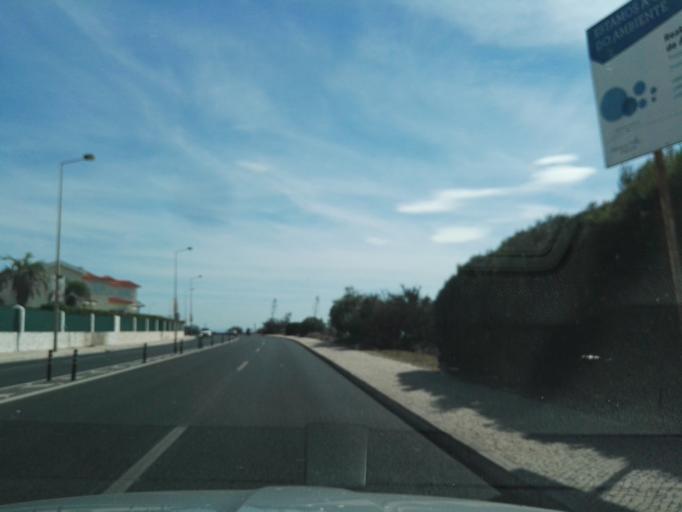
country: PT
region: Lisbon
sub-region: Cascais
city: Parede
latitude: 38.6908
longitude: -9.3639
